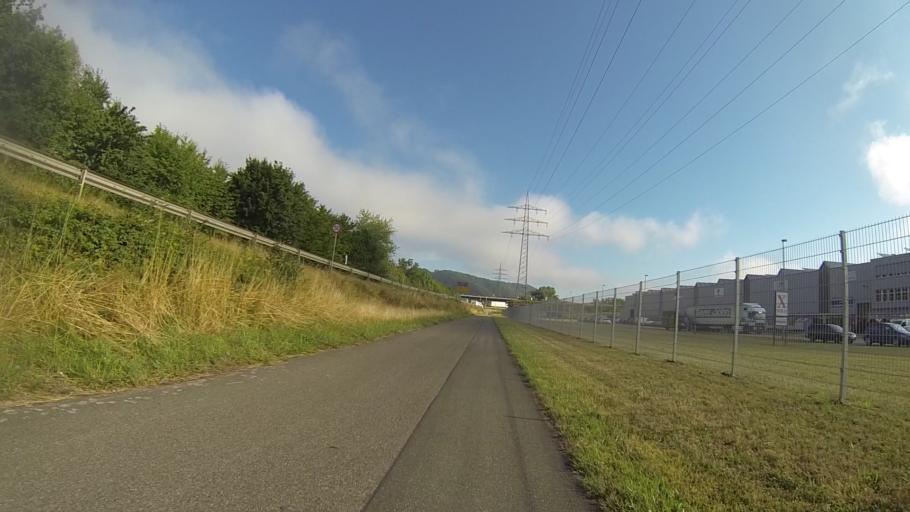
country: DE
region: Rheinland-Pfalz
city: Kenn
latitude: 49.8002
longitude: 6.6897
